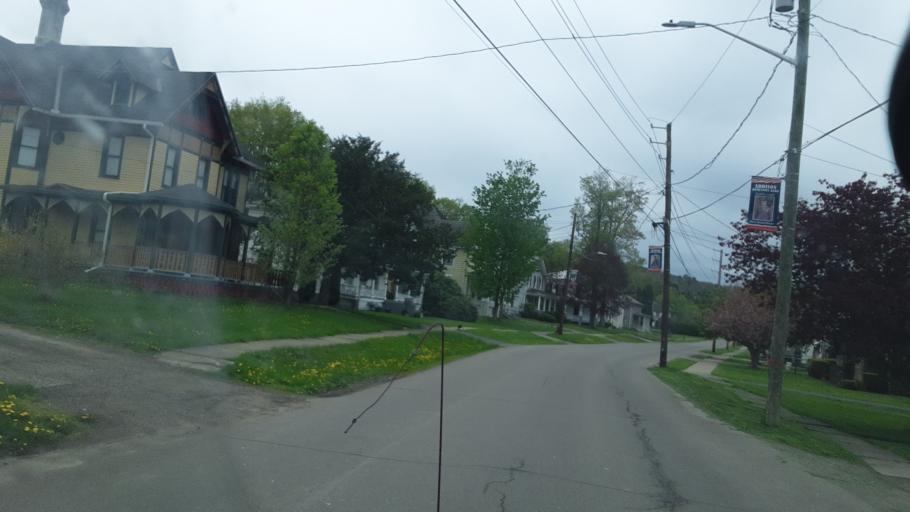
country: US
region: New York
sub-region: Steuben County
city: Addison
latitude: 42.1045
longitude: -77.2373
